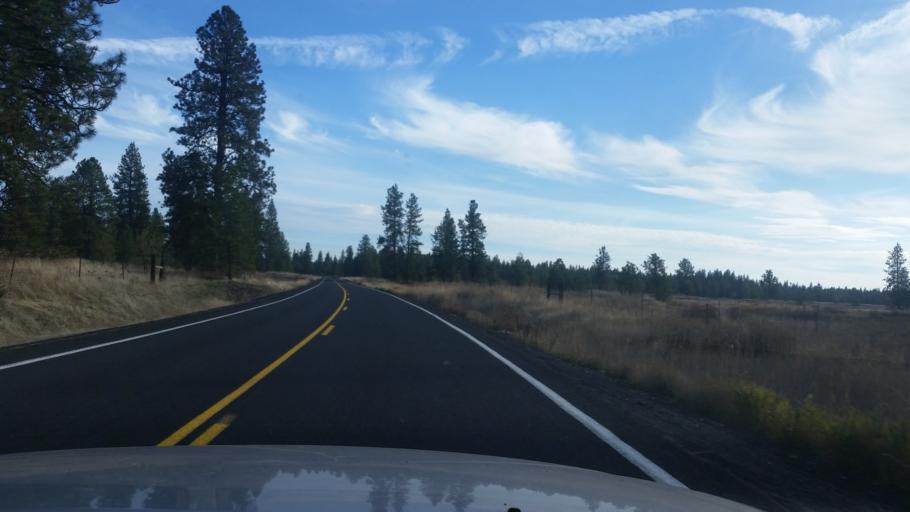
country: US
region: Washington
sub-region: Spokane County
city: Cheney
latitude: 47.4410
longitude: -117.5747
